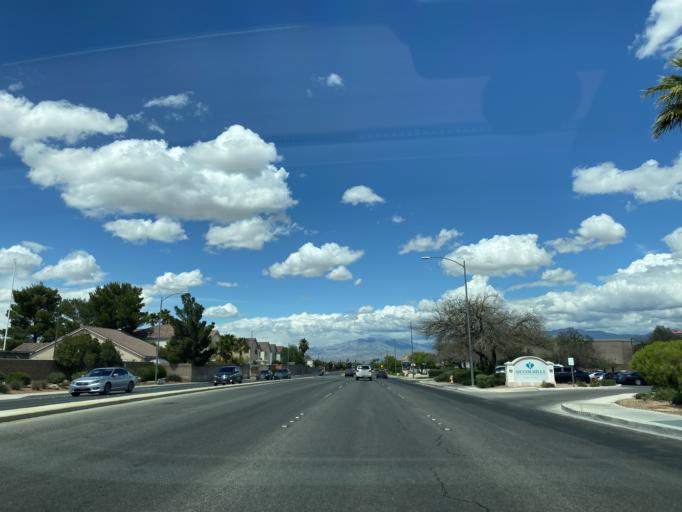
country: US
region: Nevada
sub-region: Clark County
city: Spring Valley
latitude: 36.2227
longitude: -115.2605
